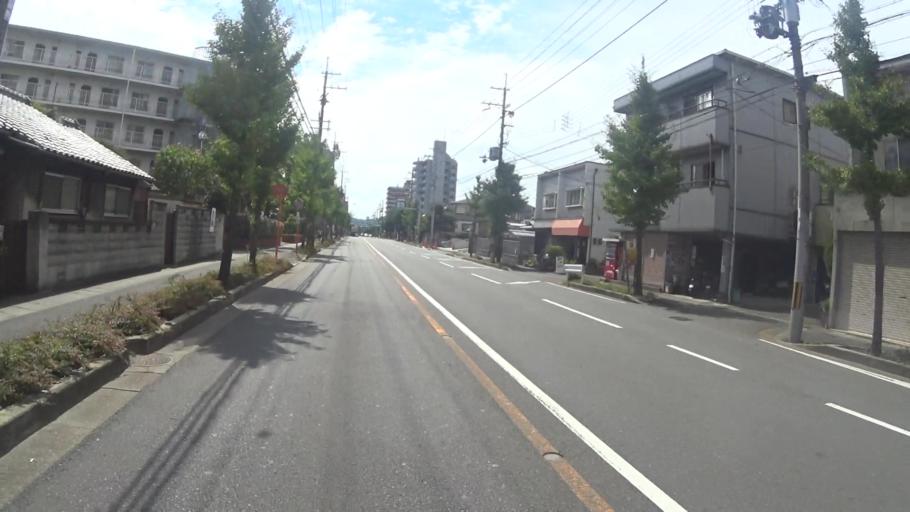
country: JP
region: Kyoto
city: Yawata
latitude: 34.9064
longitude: 135.7175
